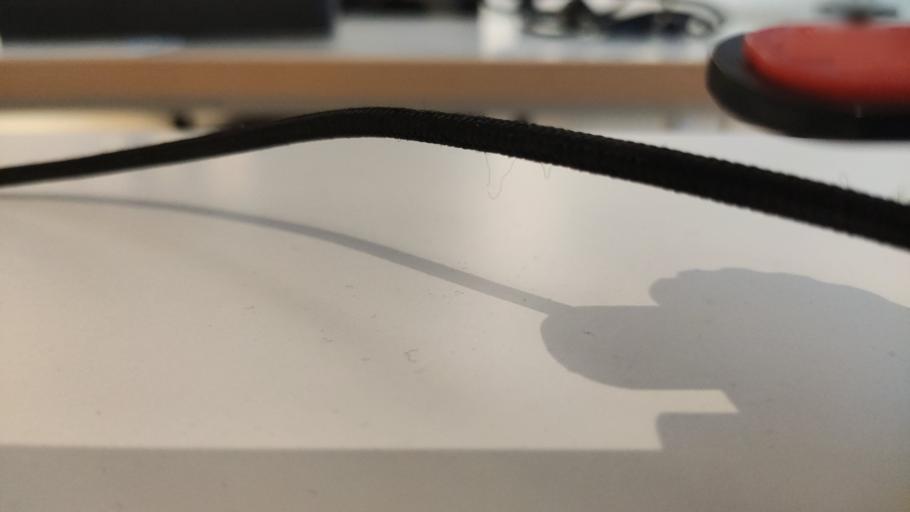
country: RU
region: Moskovskaya
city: Ruza
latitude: 55.7848
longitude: 36.2764
